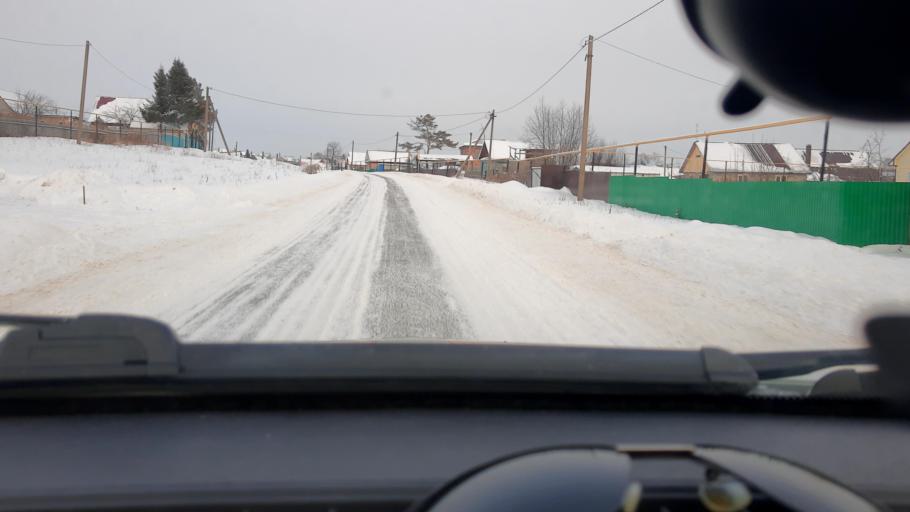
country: RU
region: Bashkortostan
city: Yazykovo
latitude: 55.0269
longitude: 56.2188
